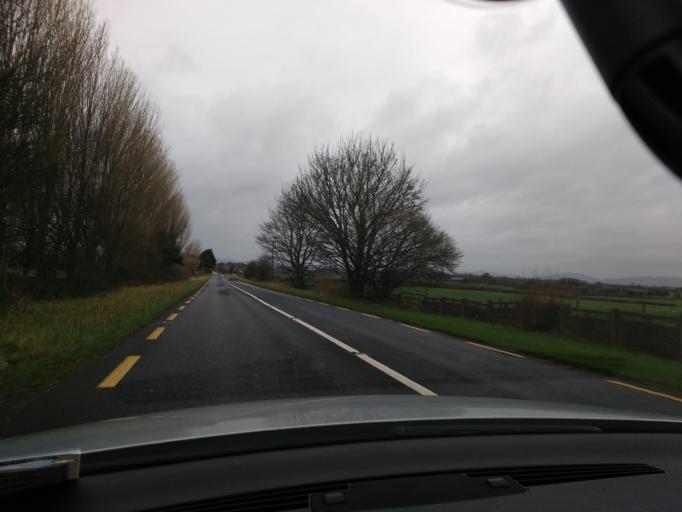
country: IE
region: Munster
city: Thurles
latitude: 52.6737
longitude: -7.7611
